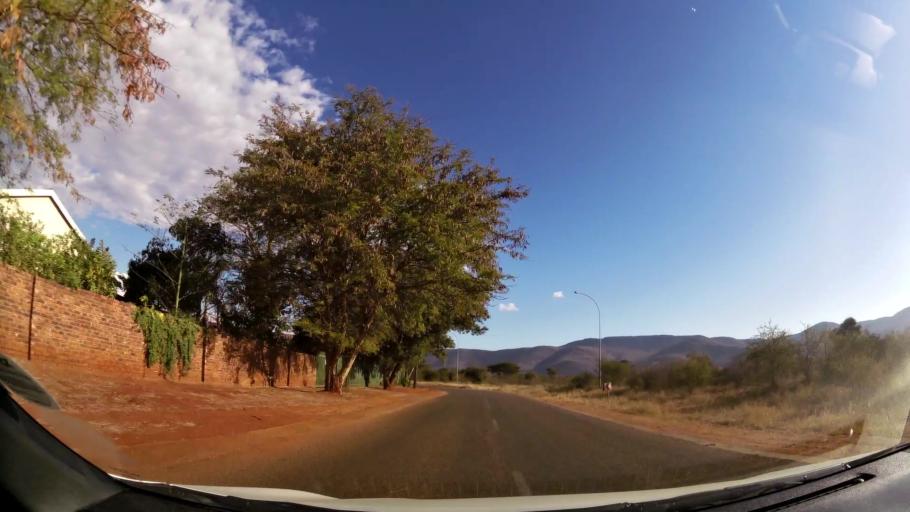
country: ZA
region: Limpopo
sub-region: Waterberg District Municipality
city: Mokopane
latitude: -24.2045
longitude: 28.9999
